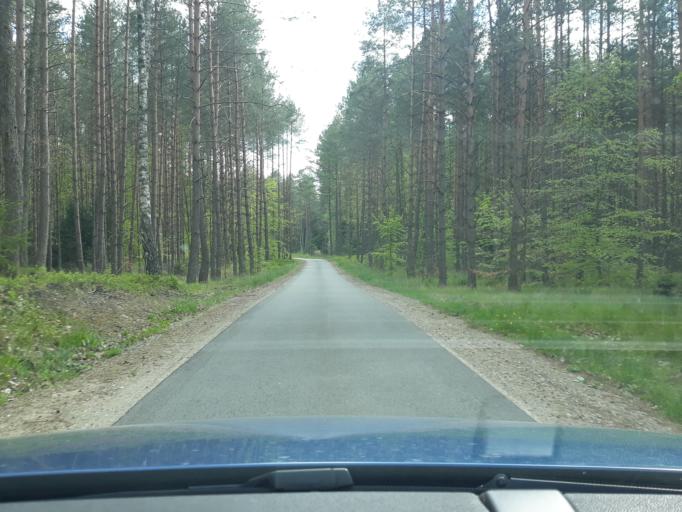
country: PL
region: Pomeranian Voivodeship
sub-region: Powiat czluchowski
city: Czluchow
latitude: 53.7374
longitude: 17.3436
